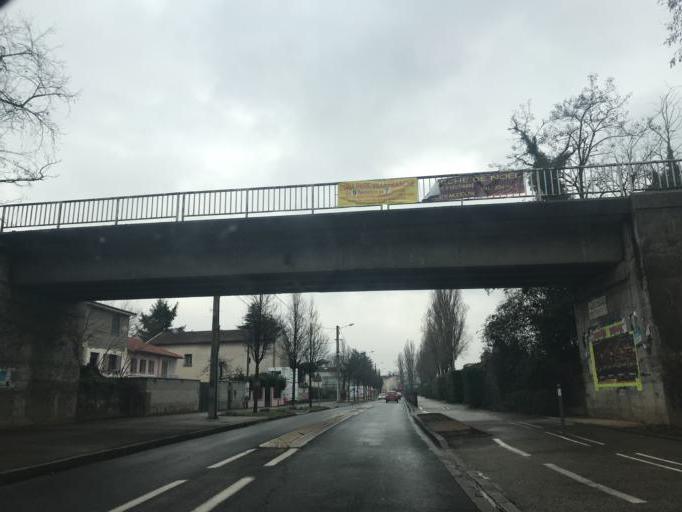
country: FR
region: Rhone-Alpes
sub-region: Departement du Rhone
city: Genay
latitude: 45.8842
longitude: 4.8335
